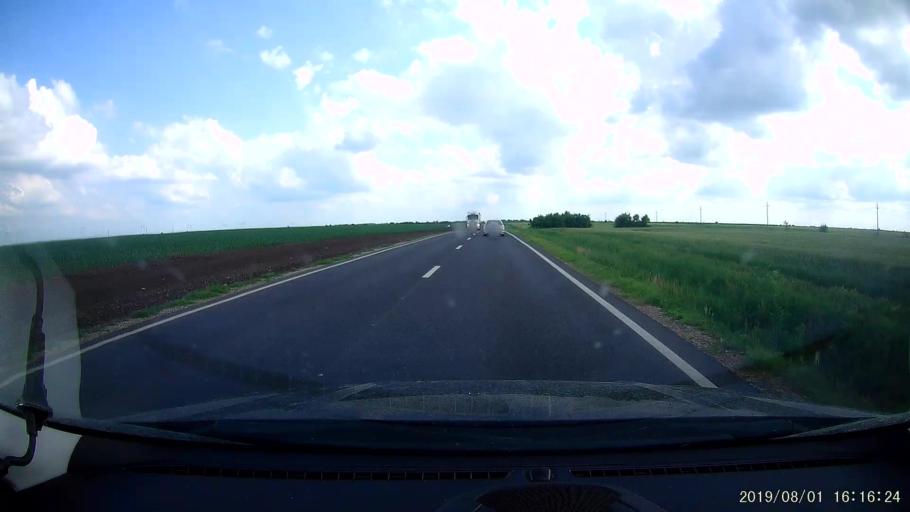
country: RO
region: Calarasi
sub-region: Comuna Stefan Voda
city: Stefan Voda
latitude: 44.3203
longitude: 27.3581
